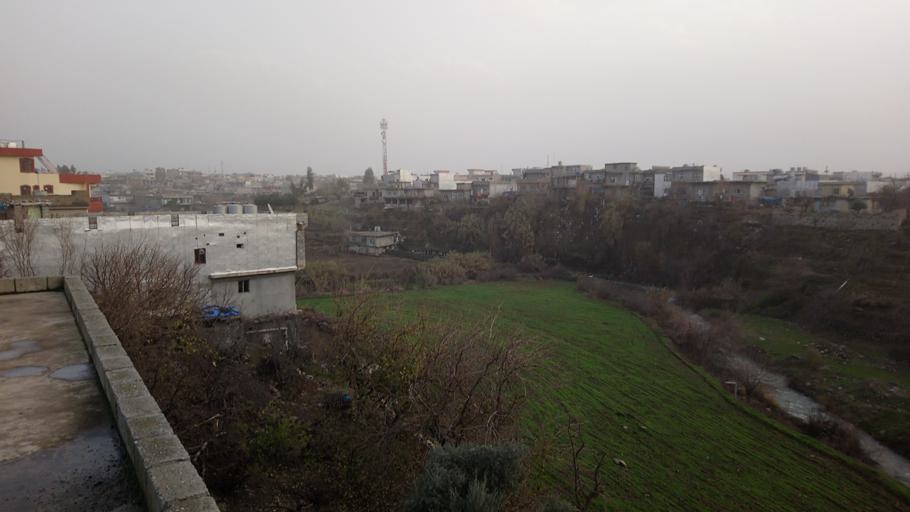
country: IQ
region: As Sulaymaniyah
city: Qeladize
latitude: 36.1818
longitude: 45.1247
